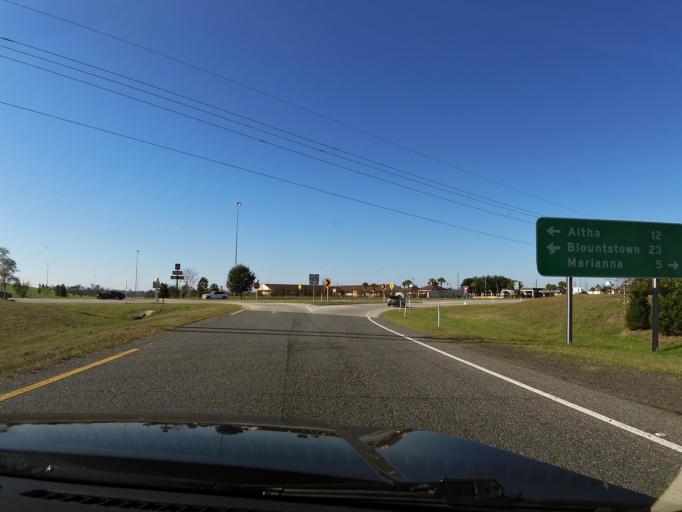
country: US
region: Florida
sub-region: Jackson County
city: Marianna
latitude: 30.7220
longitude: -85.1846
